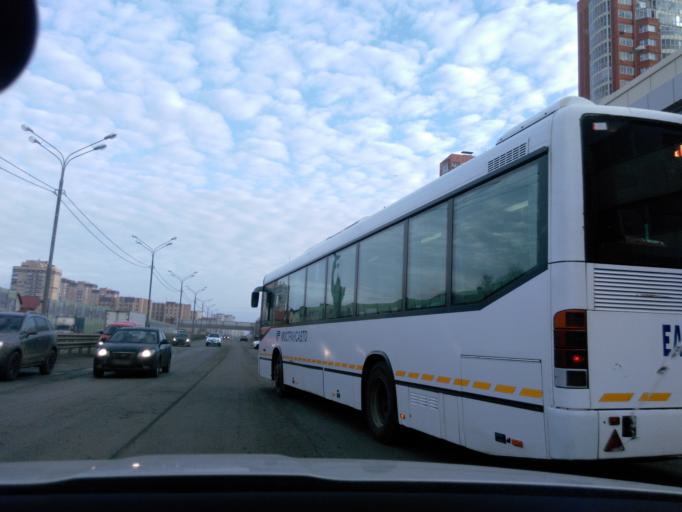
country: RU
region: Moskovskaya
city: Dolgoprudnyy
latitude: 55.9317
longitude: 37.4931
